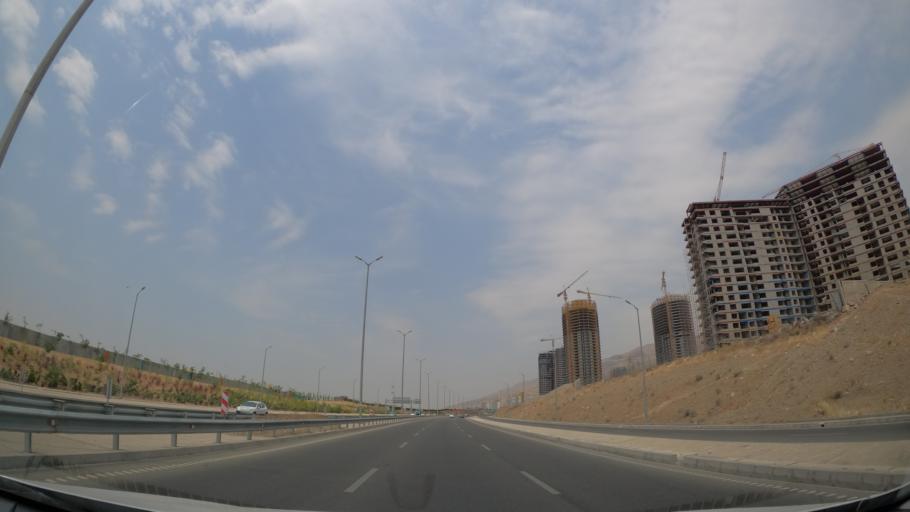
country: IR
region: Tehran
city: Shahr-e Qods
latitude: 35.7465
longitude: 51.1837
